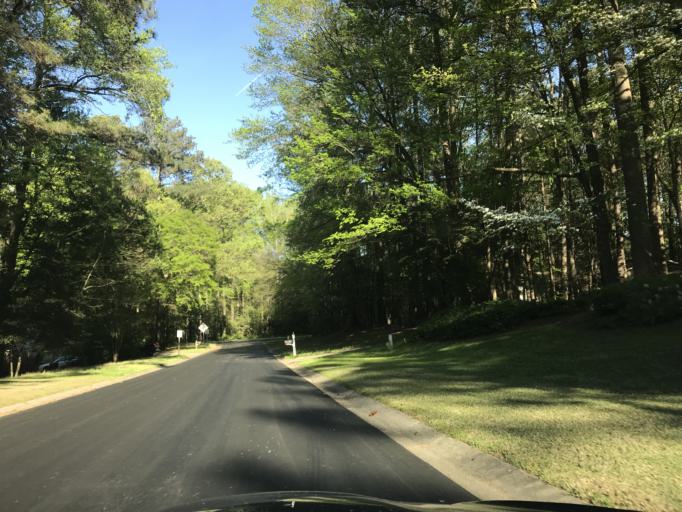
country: US
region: North Carolina
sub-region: Wake County
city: Knightdale
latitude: 35.8257
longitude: -78.5568
